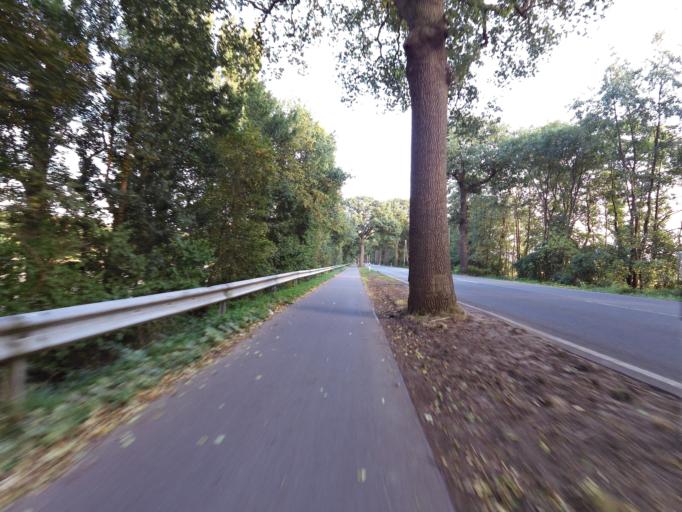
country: NL
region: Gelderland
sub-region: Gemeente Zevenaar
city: Zevenaar
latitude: 51.8977
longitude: 6.1382
